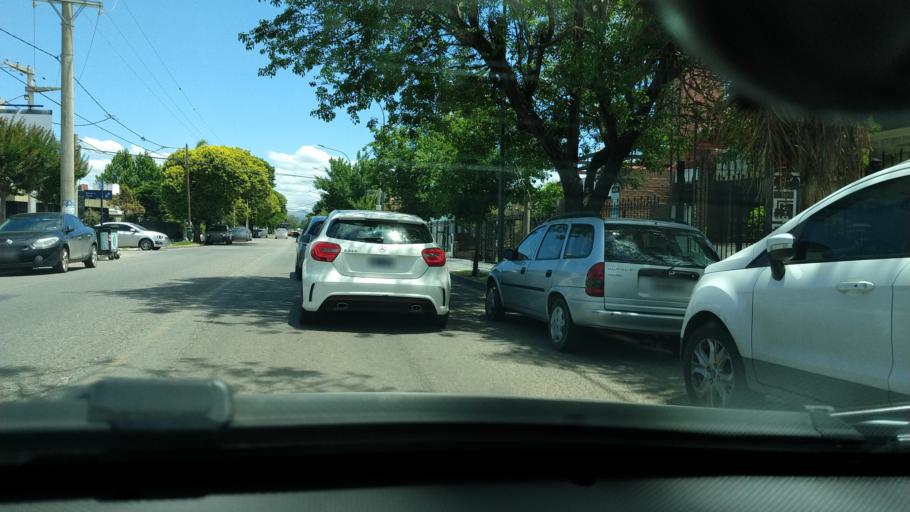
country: AR
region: Cordoba
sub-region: Departamento de Capital
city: Cordoba
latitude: -31.3616
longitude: -64.2309
